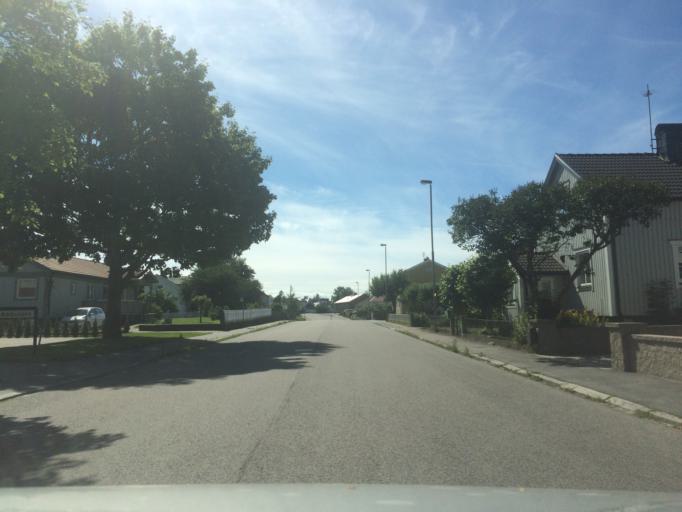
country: SE
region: Vaestra Goetaland
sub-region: Trollhattan
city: Trollhattan
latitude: 58.2882
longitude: 12.3196
